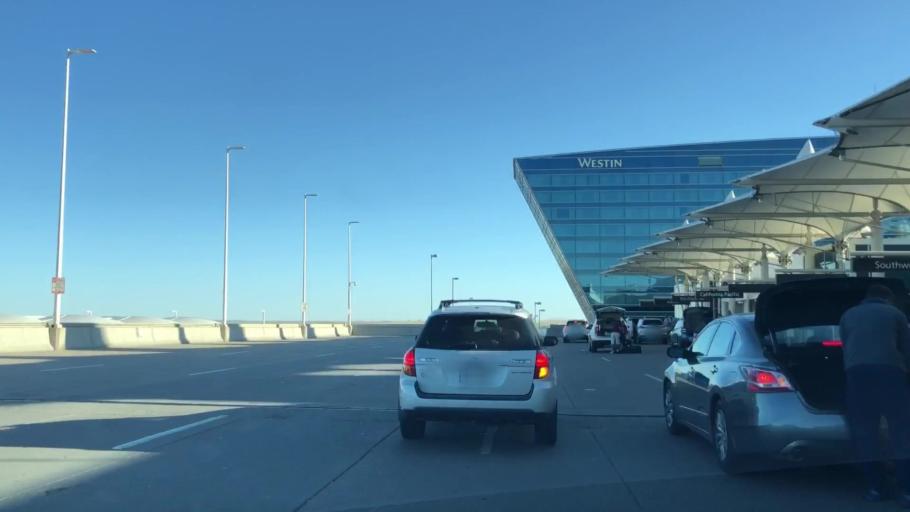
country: US
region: Colorado
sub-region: Weld County
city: Lochbuie
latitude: 39.8491
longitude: -104.6728
